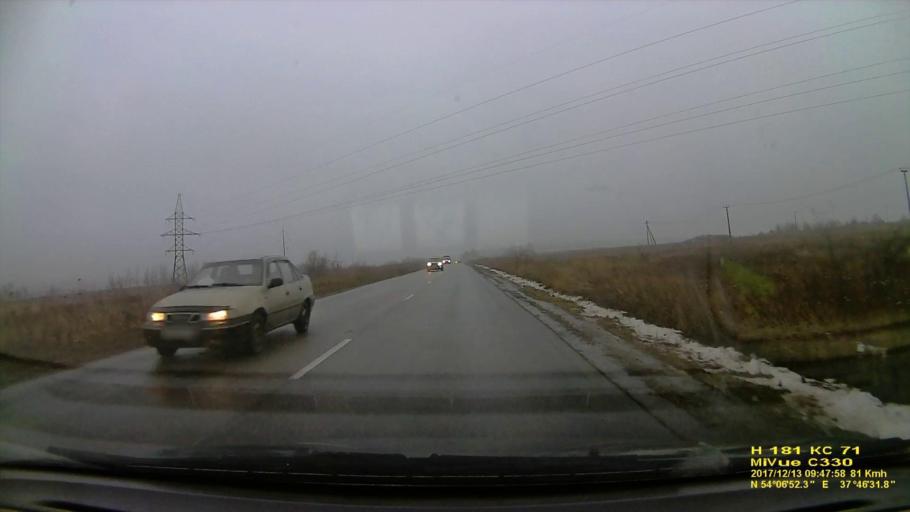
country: RU
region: Tula
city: Bolokhovo
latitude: 54.1145
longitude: 37.7756
